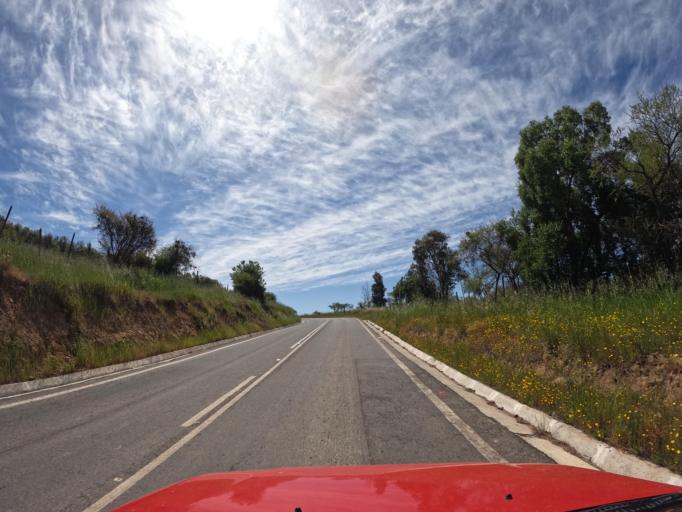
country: CL
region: Maule
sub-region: Provincia de Talca
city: Talca
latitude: -35.0175
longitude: -71.7721
